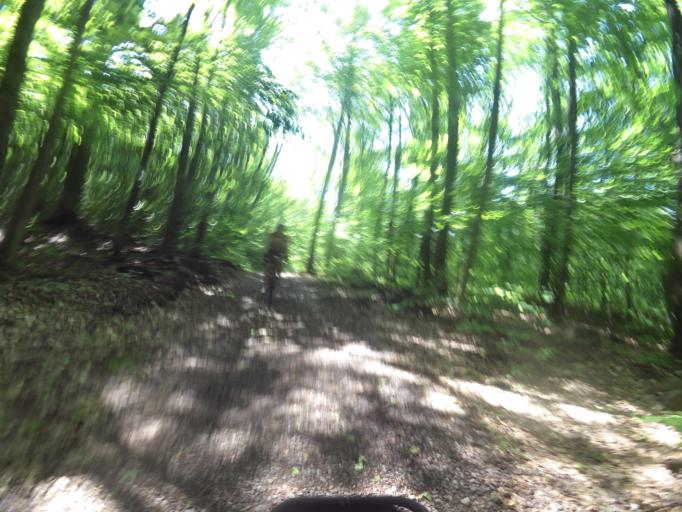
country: CA
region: Quebec
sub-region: Outaouais
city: Wakefield
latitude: 45.5501
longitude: -75.8929
